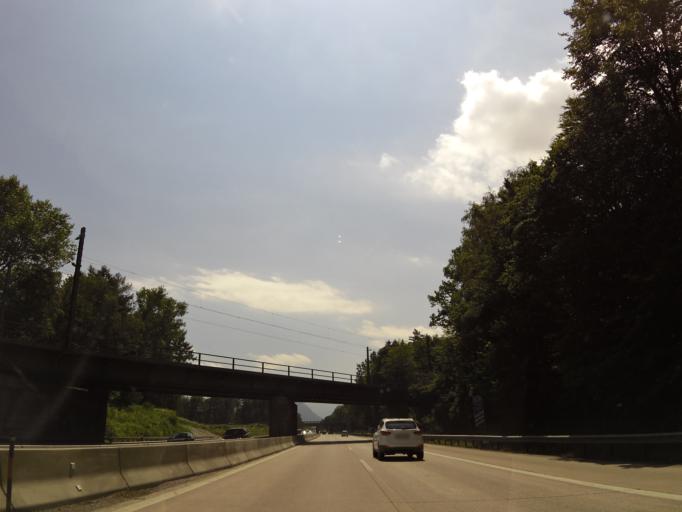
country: DE
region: Bavaria
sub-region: Upper Bavaria
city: Brannenburg
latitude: 47.7638
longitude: 12.1035
